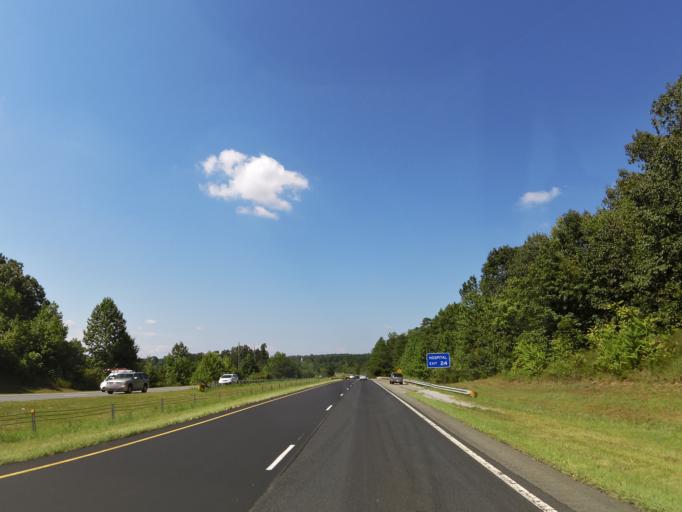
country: US
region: North Carolina
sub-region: Lincoln County
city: Lincolnton
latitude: 35.4604
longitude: -81.2194
